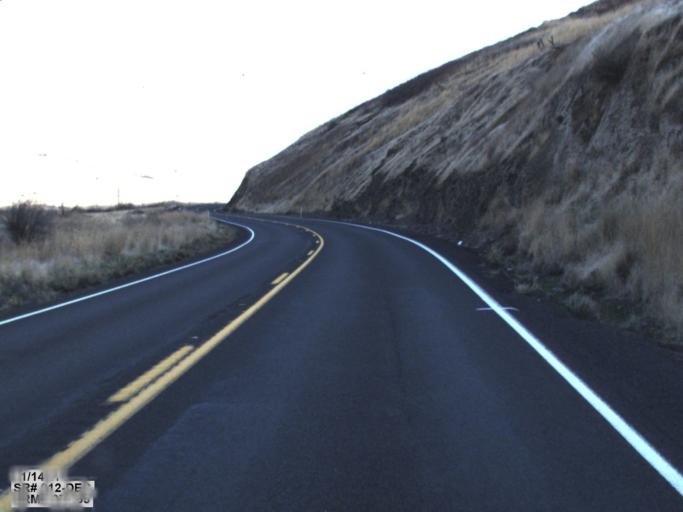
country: US
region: Washington
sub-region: Columbia County
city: Dayton
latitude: 46.4478
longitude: -117.9569
